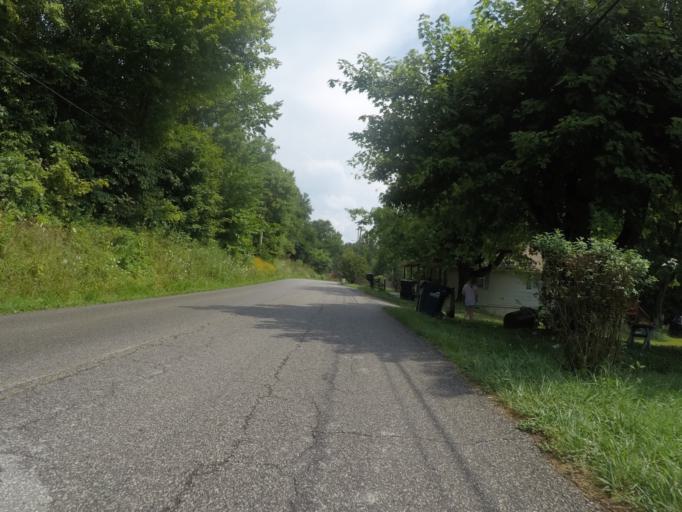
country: US
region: Kentucky
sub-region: Boyd County
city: Ironville
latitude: 38.4581
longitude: -82.6766
